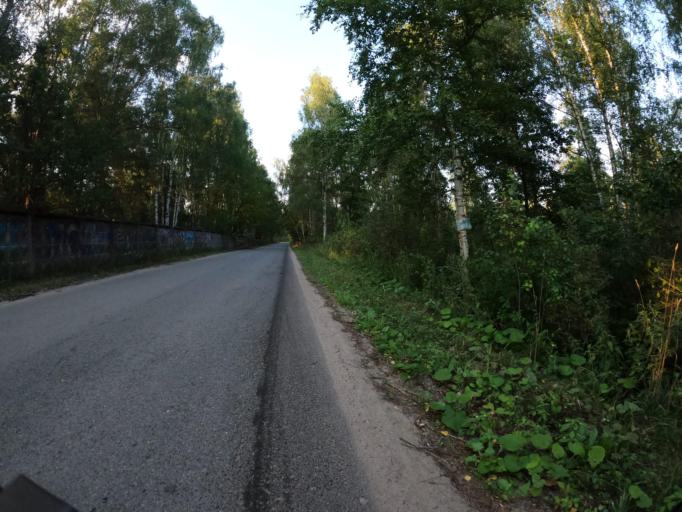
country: RU
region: Moskovskaya
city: Malyshevo
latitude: 55.5201
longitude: 38.2942
